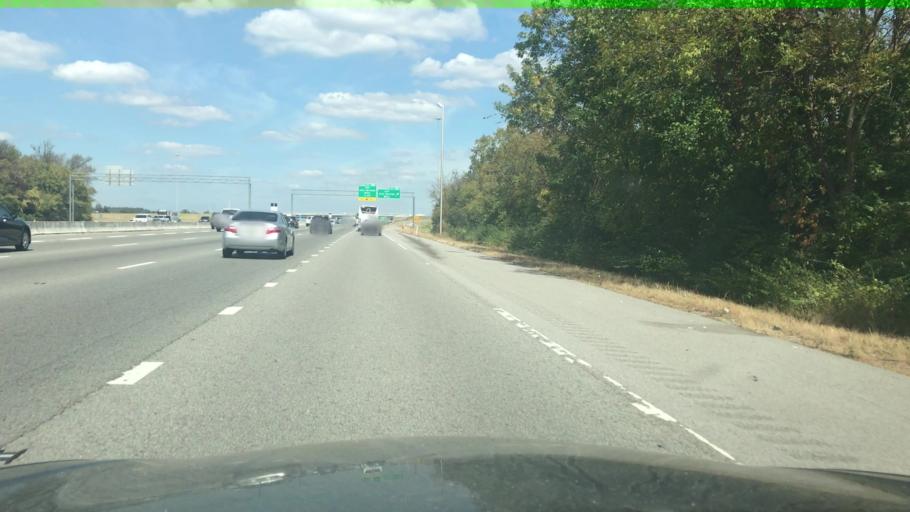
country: US
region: Tennessee
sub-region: Williamson County
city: Franklin
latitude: 35.9423
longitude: -86.8158
